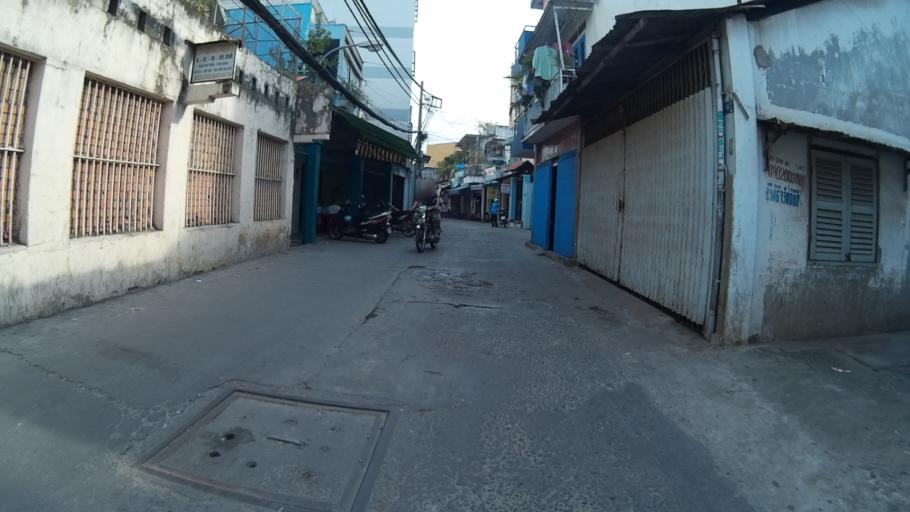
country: VN
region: Ho Chi Minh City
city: Quan Binh Thanh
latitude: 10.8023
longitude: 106.7026
